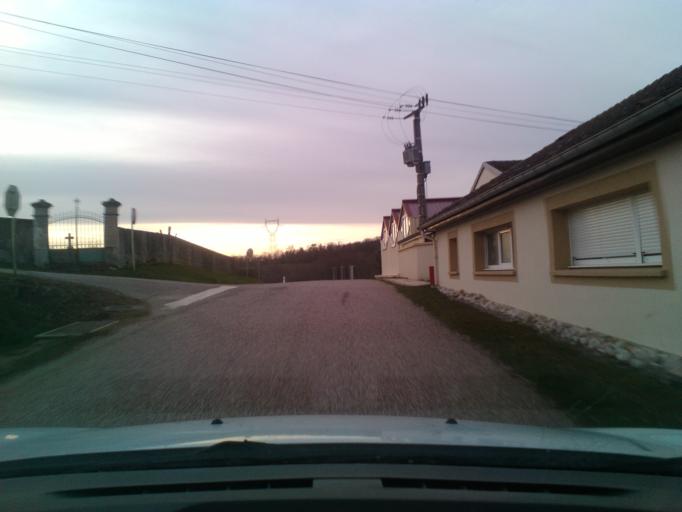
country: FR
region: Lorraine
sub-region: Departement des Vosges
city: Portieux
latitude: 48.3486
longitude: 6.3674
